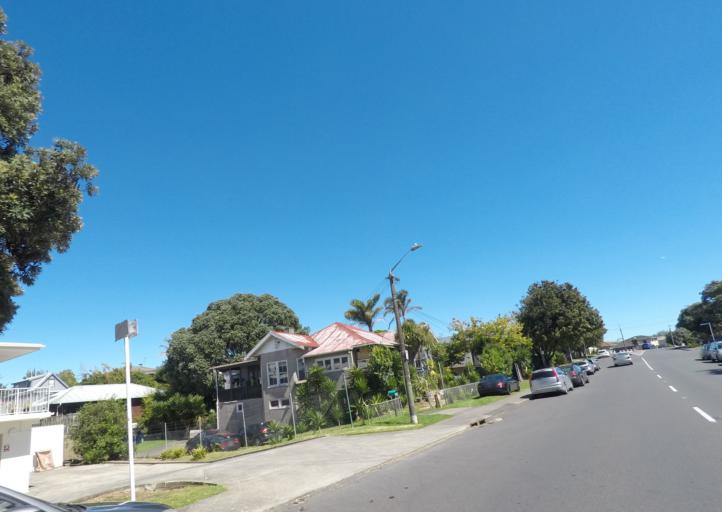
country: NZ
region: Auckland
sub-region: Auckland
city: Auckland
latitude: -36.8788
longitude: 174.7349
